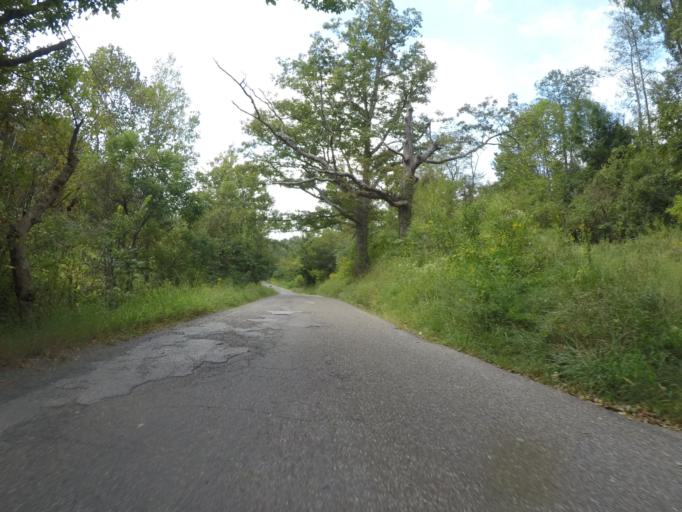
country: US
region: West Virginia
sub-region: Cabell County
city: Huntington
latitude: 38.4502
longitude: -82.4274
